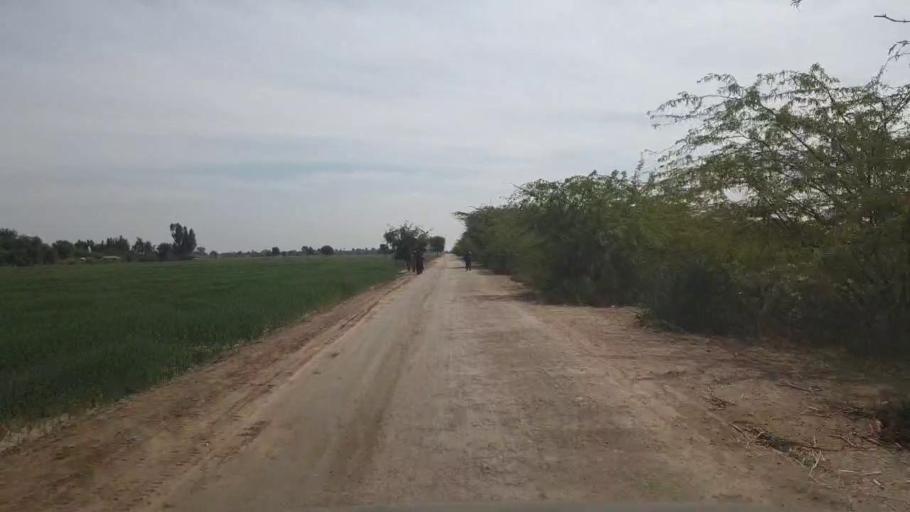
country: PK
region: Sindh
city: Kunri
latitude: 25.2838
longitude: 69.5950
